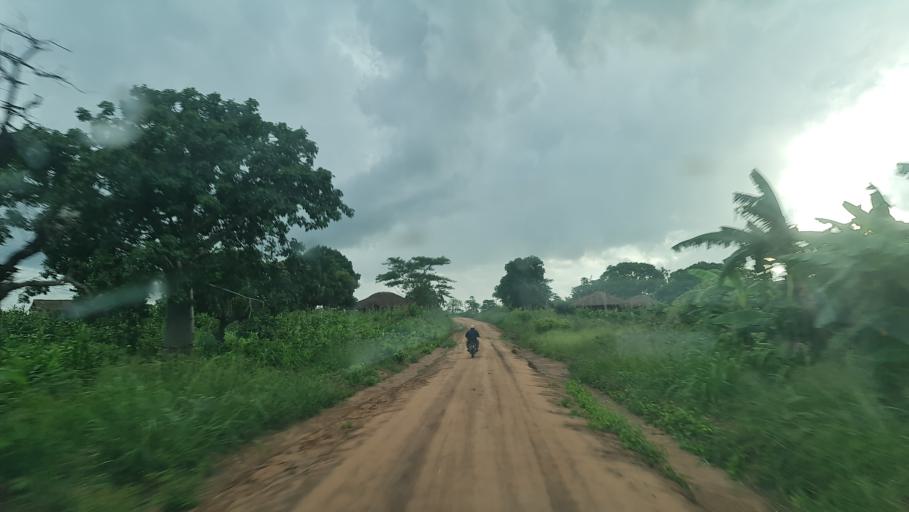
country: MZ
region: Nampula
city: Nacala
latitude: -13.9926
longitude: 40.3682
